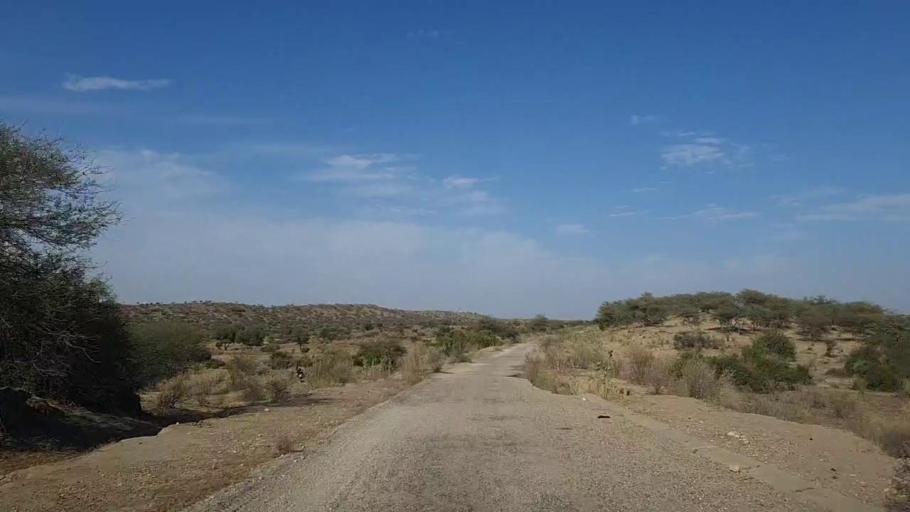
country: PK
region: Sindh
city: Naukot
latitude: 24.8487
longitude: 69.5345
